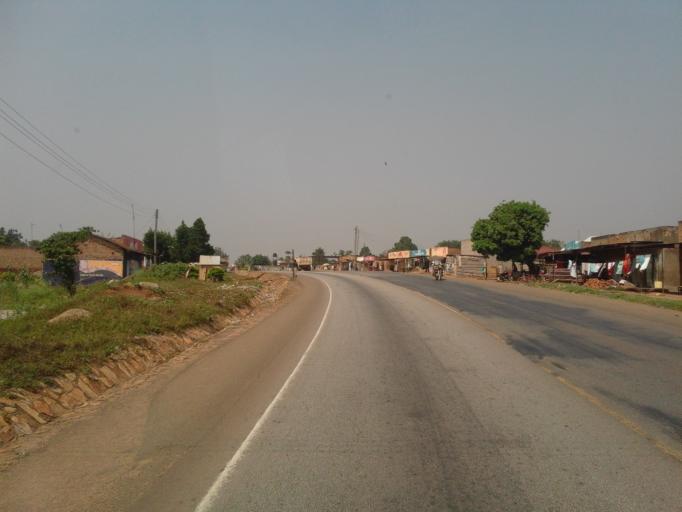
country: UG
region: Eastern Region
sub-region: Iganga District
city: Iganga
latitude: 0.6290
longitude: 33.5195
